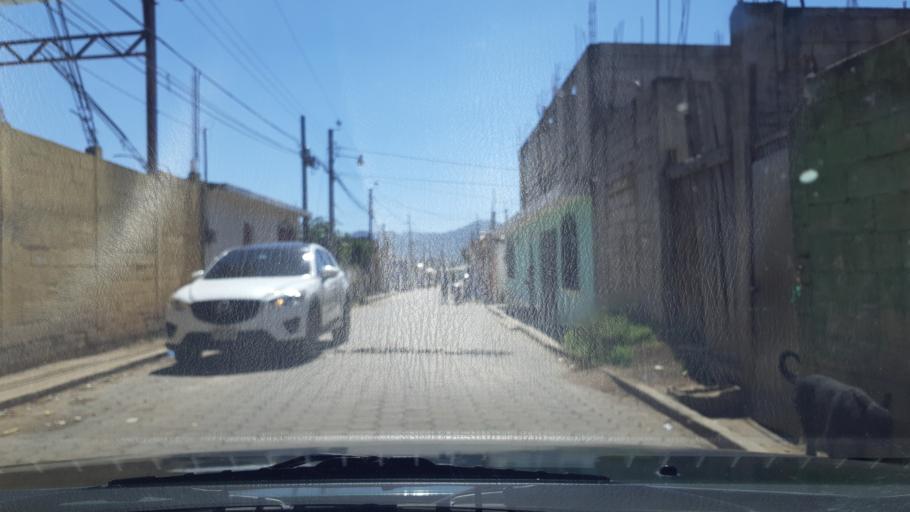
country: GT
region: Chimaltenango
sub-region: Municipio de Zaragoza
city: Zaragoza
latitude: 14.6620
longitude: -90.8632
